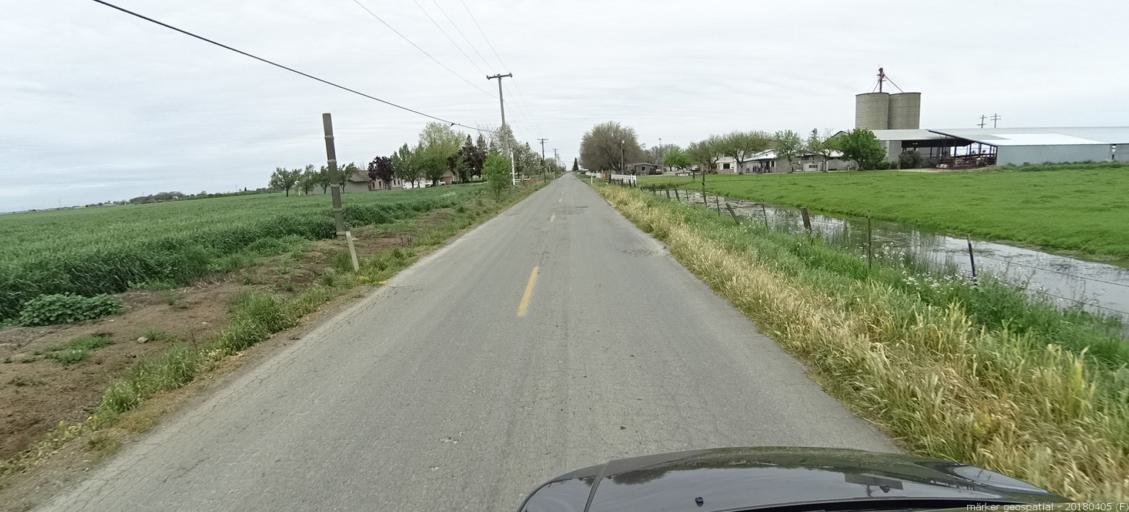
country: US
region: California
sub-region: Sacramento County
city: Elk Grove
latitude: 38.3402
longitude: -121.3989
